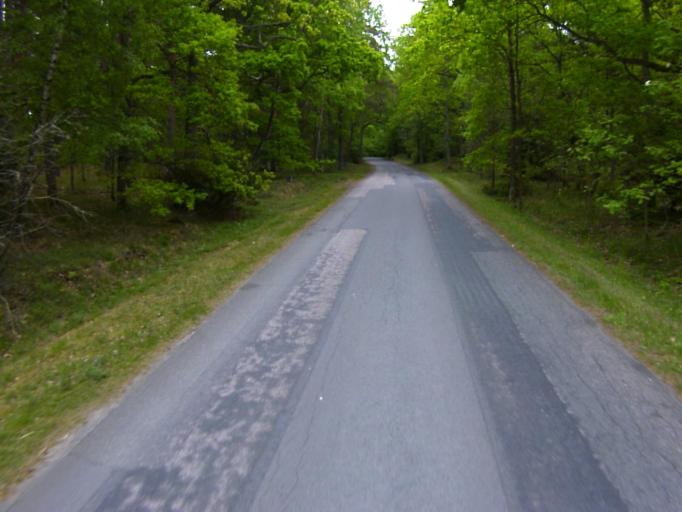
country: SE
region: Skane
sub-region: Kristianstads Kommun
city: Ahus
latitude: 55.9230
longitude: 14.3098
